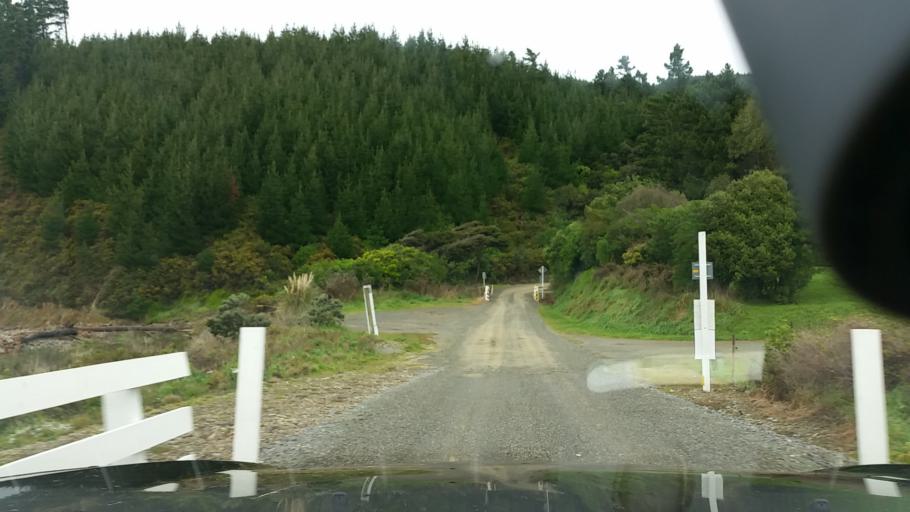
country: NZ
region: Marlborough
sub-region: Marlborough District
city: Picton
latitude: -41.3584
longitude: 174.0706
